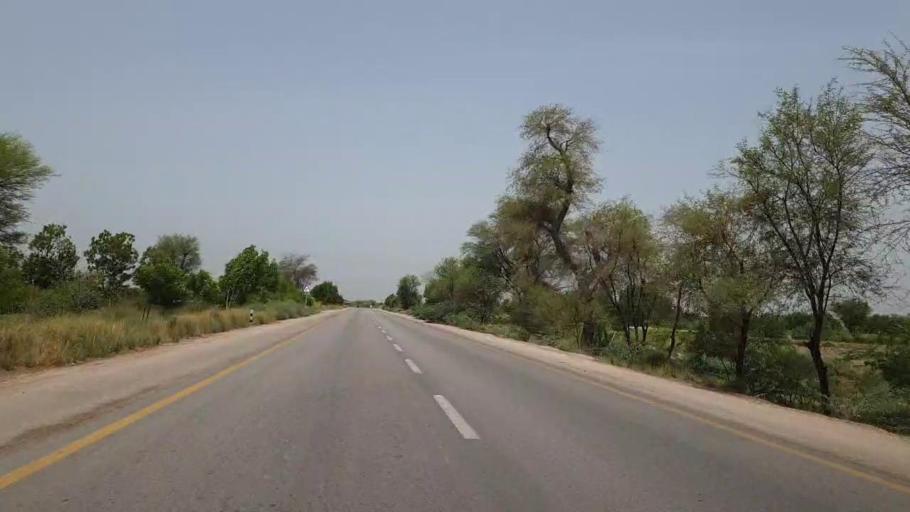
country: PK
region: Sindh
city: Nawabshah
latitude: 26.2135
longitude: 68.5119
